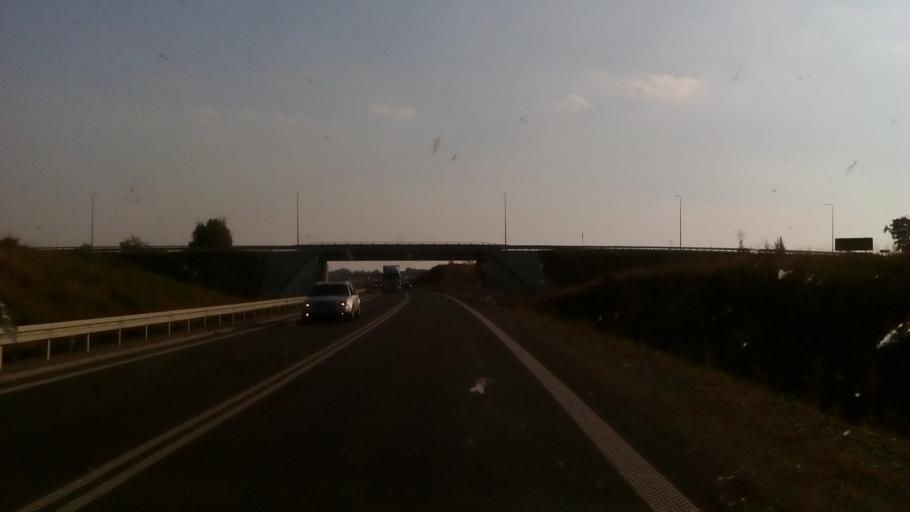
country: PL
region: Podlasie
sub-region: Powiat grajewski
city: Rajgrod
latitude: 53.7751
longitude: 22.8351
